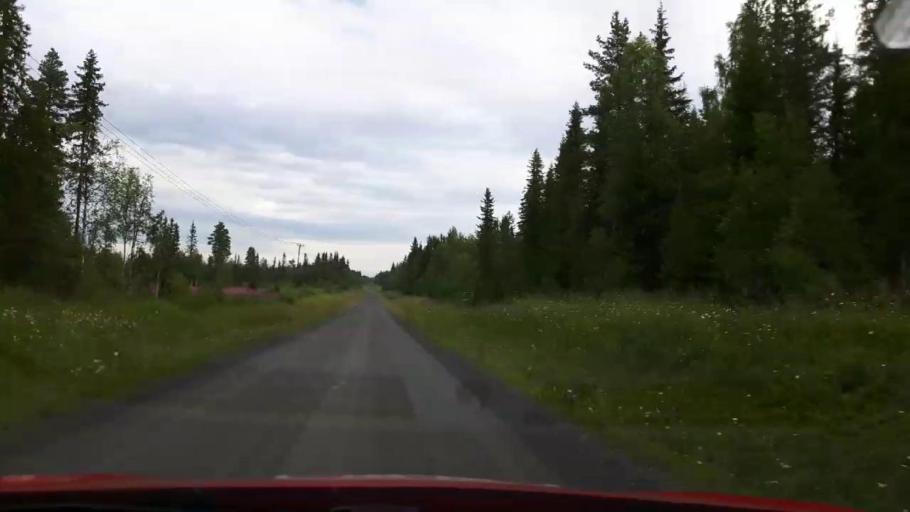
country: SE
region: Jaemtland
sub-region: Stroemsunds Kommun
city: Stroemsund
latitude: 63.5031
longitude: 15.3325
